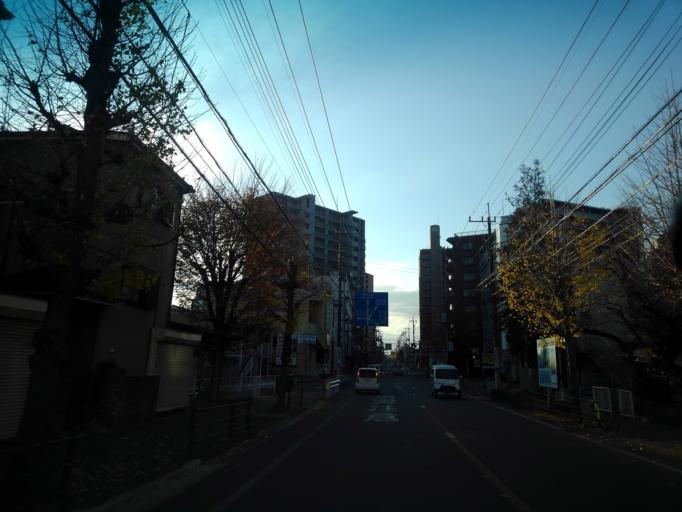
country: JP
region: Saitama
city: Tokorozawa
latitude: 35.7919
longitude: 139.4593
